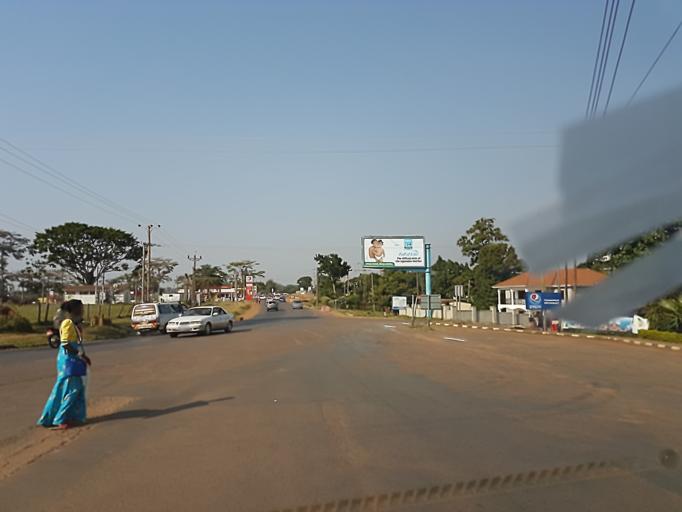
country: UG
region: Central Region
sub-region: Wakiso District
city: Entebbe
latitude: 0.0672
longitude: 32.4759
